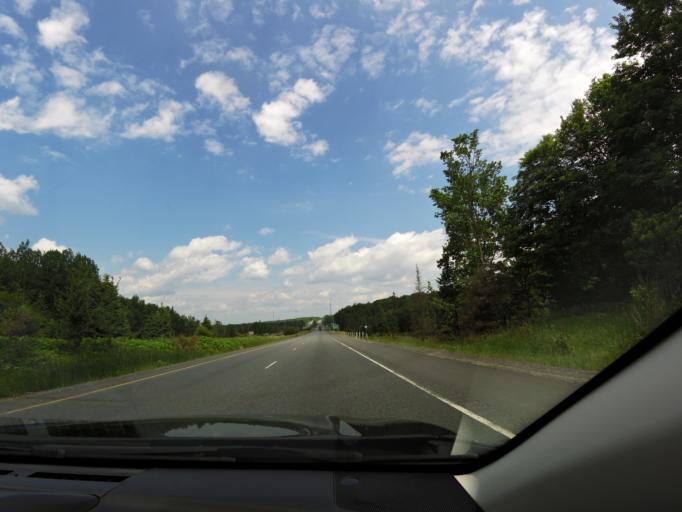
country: CA
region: Ontario
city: Bracebridge
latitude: 45.1899
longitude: -79.3127
